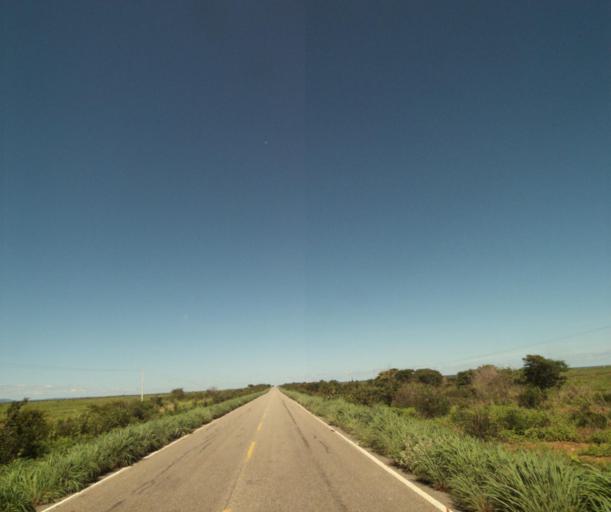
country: BR
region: Bahia
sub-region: Palmas De Monte Alto
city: Palmas de Monte Alto
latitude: -14.2712
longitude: -43.4253
